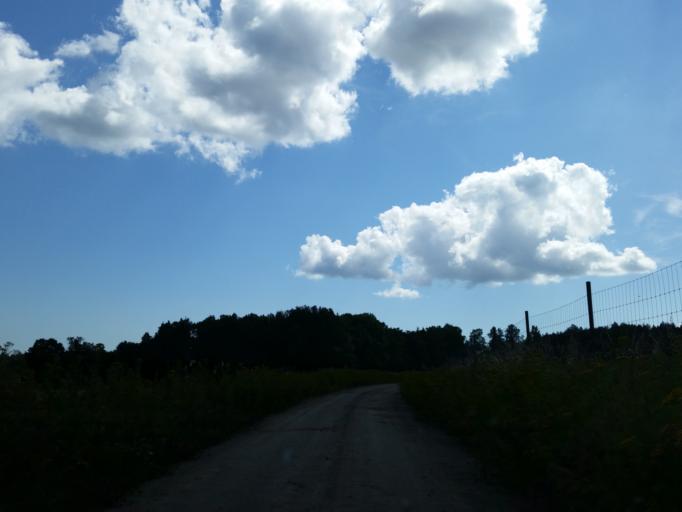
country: SE
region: Stockholm
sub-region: Sodertalje Kommun
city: Pershagen
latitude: 59.0654
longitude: 17.6614
